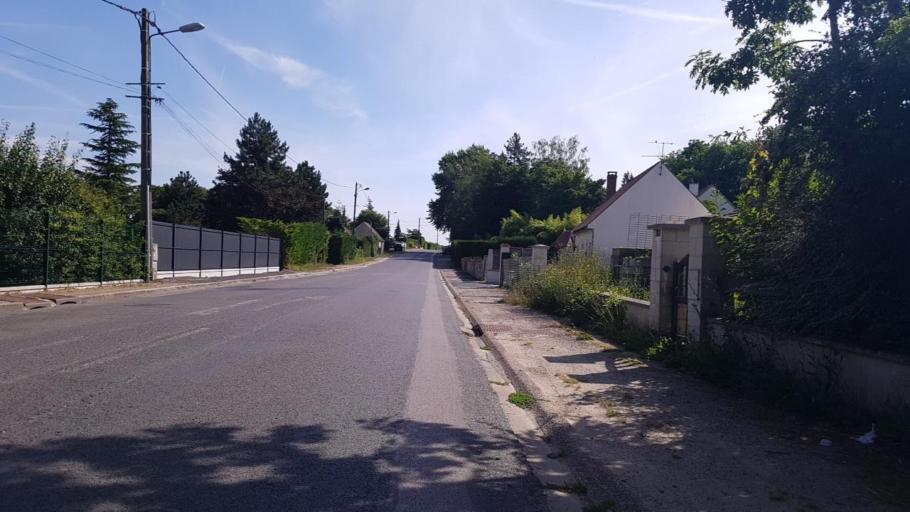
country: FR
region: Picardie
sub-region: Departement de l'Oise
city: Pontpoint
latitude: 49.3021
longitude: 2.6587
